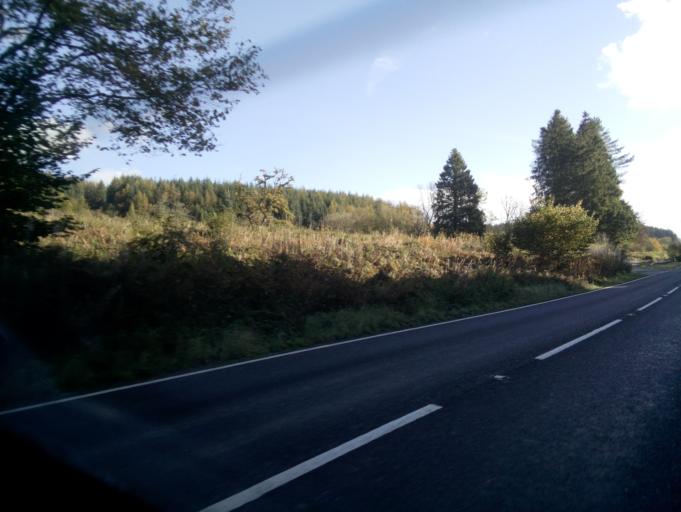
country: GB
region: Wales
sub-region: Merthyr Tydfil County Borough
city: Merthyr Tydfil
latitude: 51.8062
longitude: -3.4416
